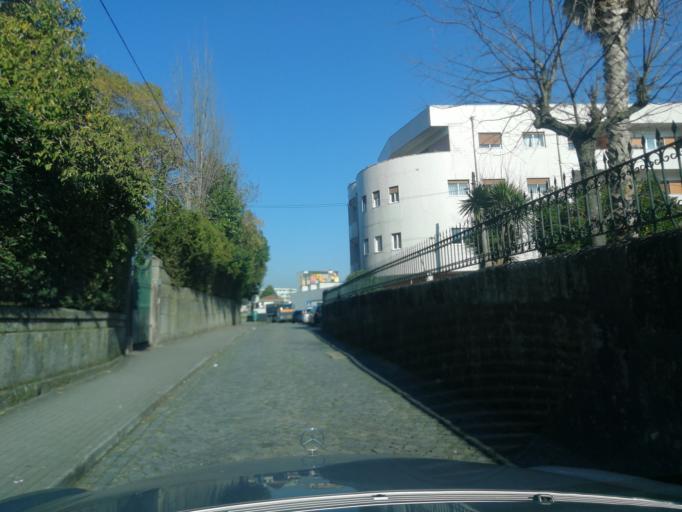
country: PT
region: Braga
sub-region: Guimaraes
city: Ponte
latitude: 41.4865
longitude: -8.3491
